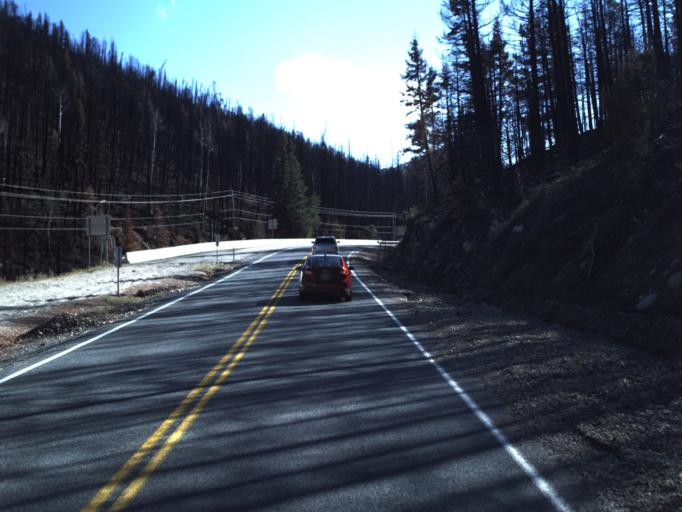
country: US
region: Utah
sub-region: Iron County
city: Parowan
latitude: 37.7307
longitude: -112.8387
